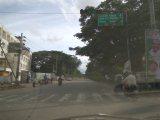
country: IN
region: Karnataka
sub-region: Bangalore Urban
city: Bangalore
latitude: 12.9902
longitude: 77.5508
